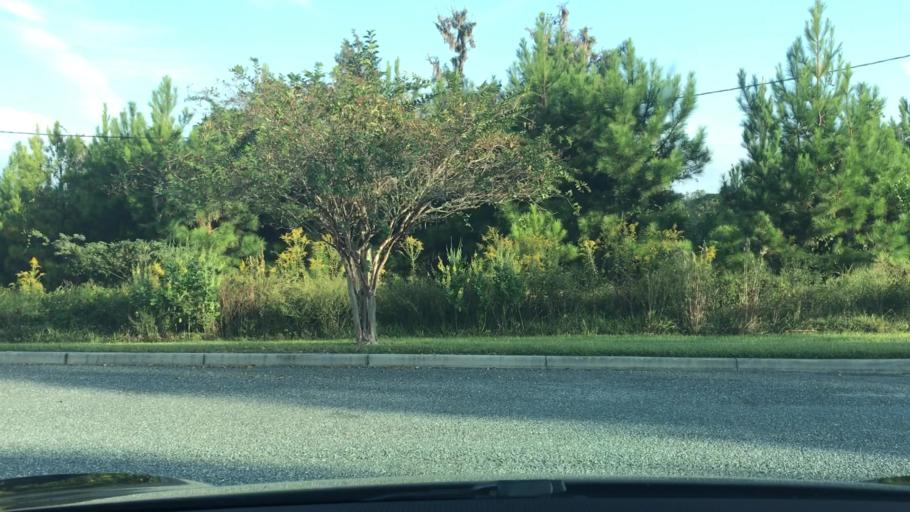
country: US
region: Florida
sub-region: Columbia County
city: Lake City
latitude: 30.1814
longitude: -82.6797
